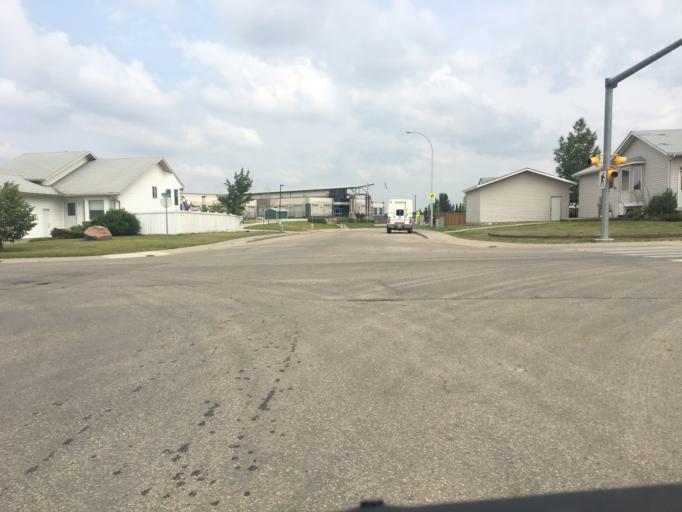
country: CA
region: Alberta
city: Grande Prairie
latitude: 55.1475
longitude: -118.8124
